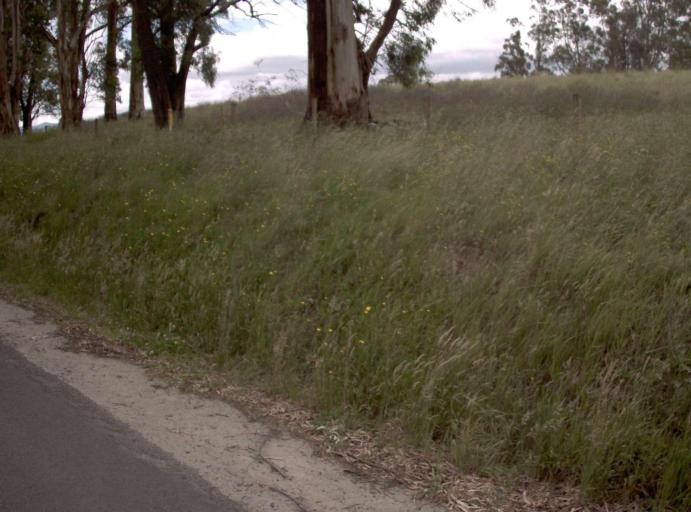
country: AU
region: Victoria
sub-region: Latrobe
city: Moe
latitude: -37.9942
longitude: 146.1462
